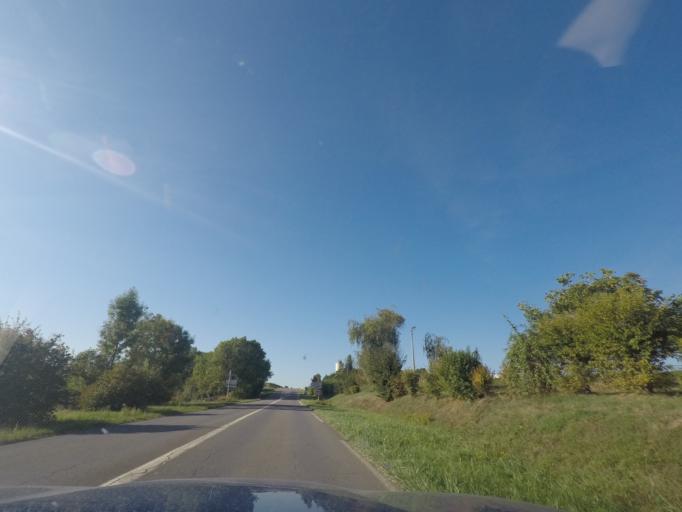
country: FR
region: Lorraine
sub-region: Departement de la Moselle
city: Hettange-Grande
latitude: 49.4526
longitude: 6.1777
